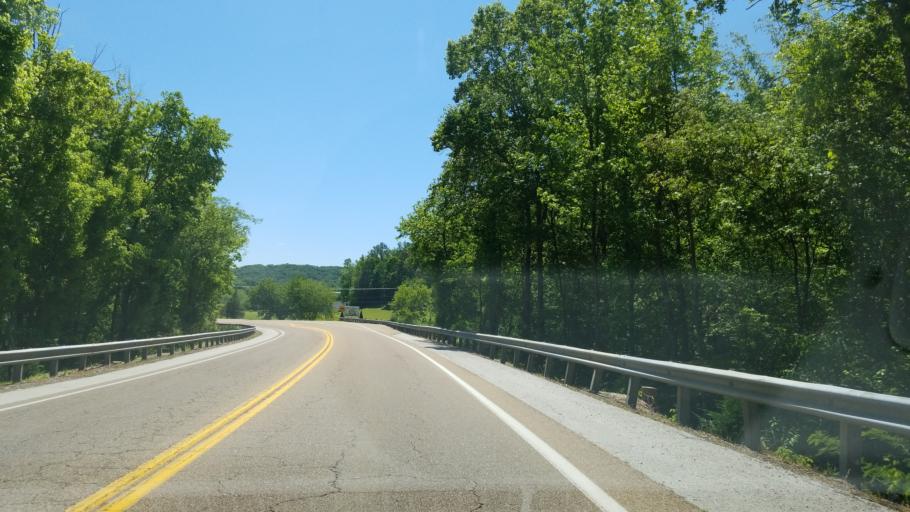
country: US
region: Tennessee
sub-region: Hamilton County
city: Collegedale
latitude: 35.0548
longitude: -85.0551
